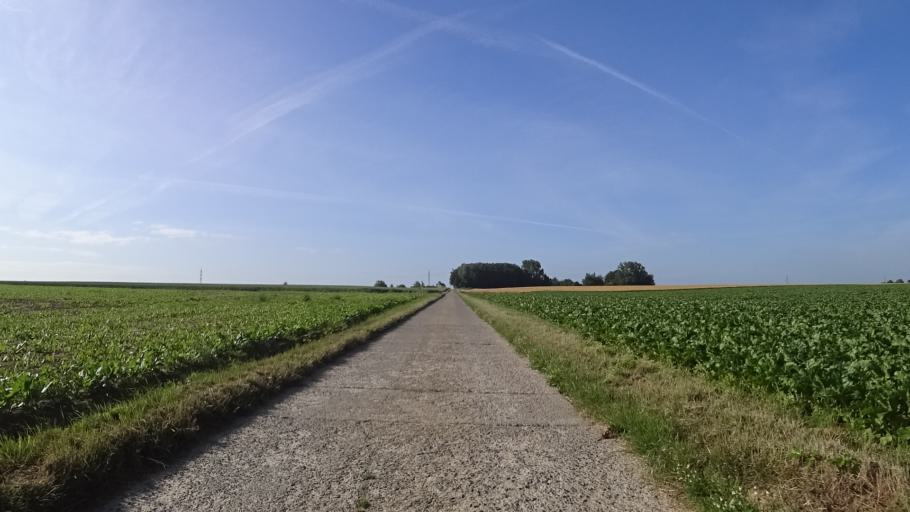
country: BE
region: Wallonia
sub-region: Province de Namur
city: Namur
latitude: 50.5288
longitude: 4.8347
